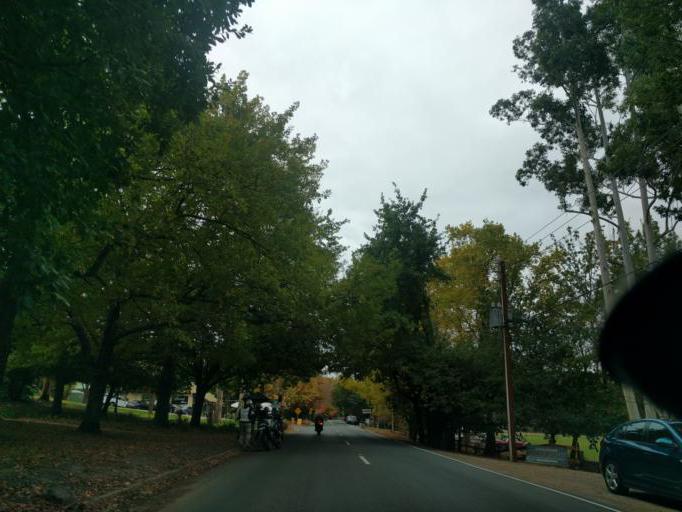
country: AU
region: South Australia
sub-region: Adelaide Hills
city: Stirling
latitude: -35.0432
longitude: 138.7600
